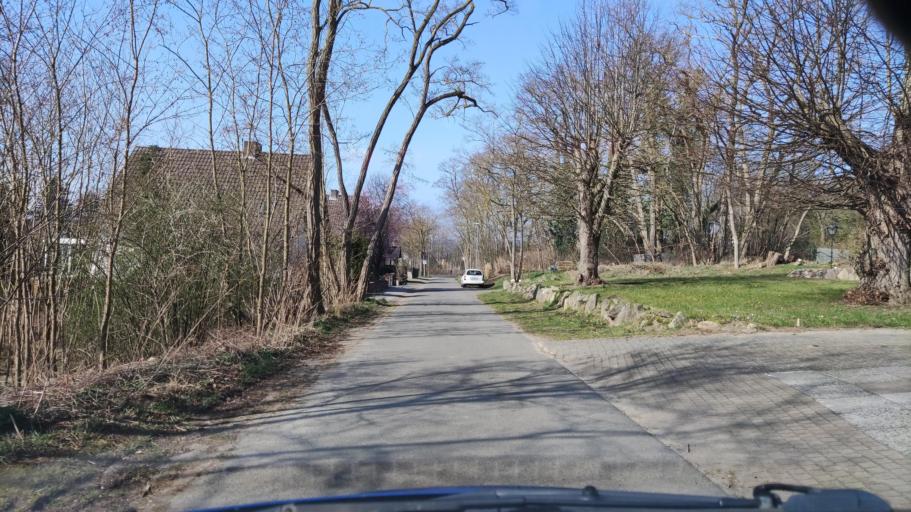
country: DE
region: Lower Saxony
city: Clenze
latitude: 52.9397
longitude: 10.9629
